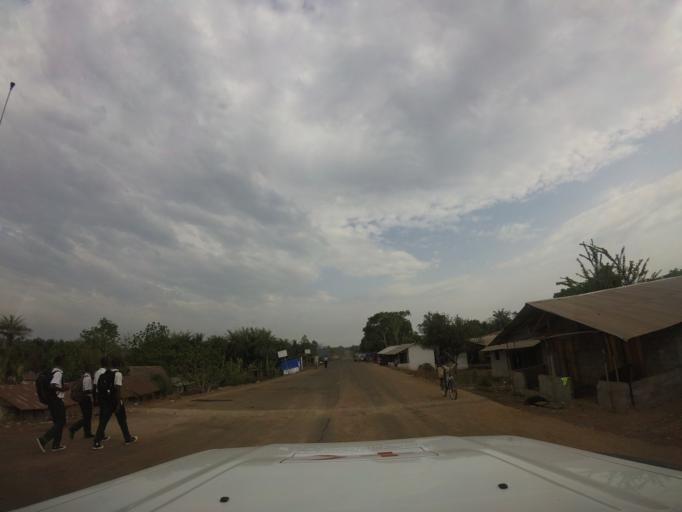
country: LR
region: Grand Cape Mount
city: Robertsport
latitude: 6.9672
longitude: -11.3128
